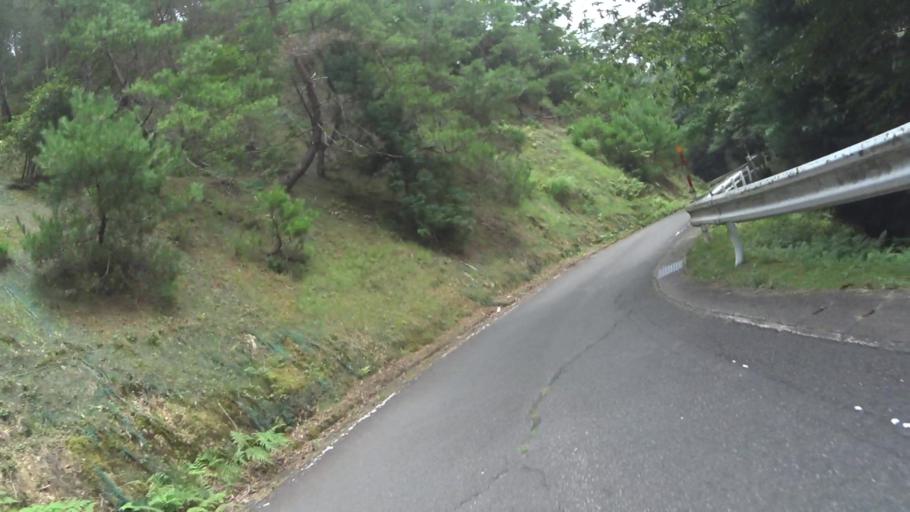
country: JP
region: Kyoto
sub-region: Kyoto-shi
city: Kamigyo-ku
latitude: 35.2051
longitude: 135.6725
